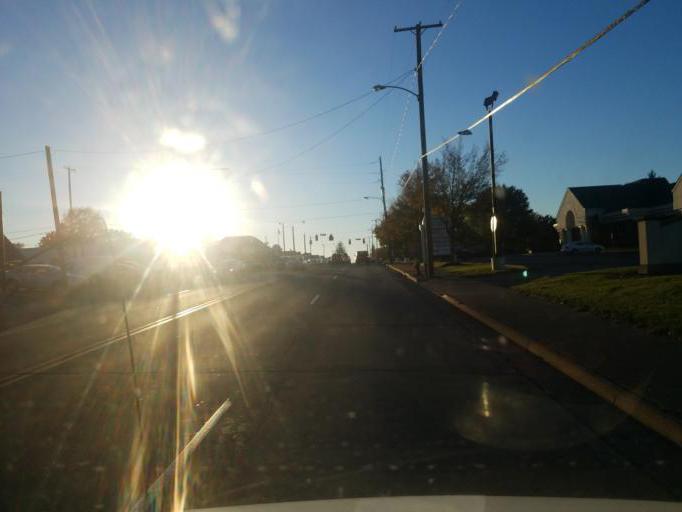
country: US
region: Ohio
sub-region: Stark County
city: Alliance
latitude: 40.9019
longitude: -81.1226
